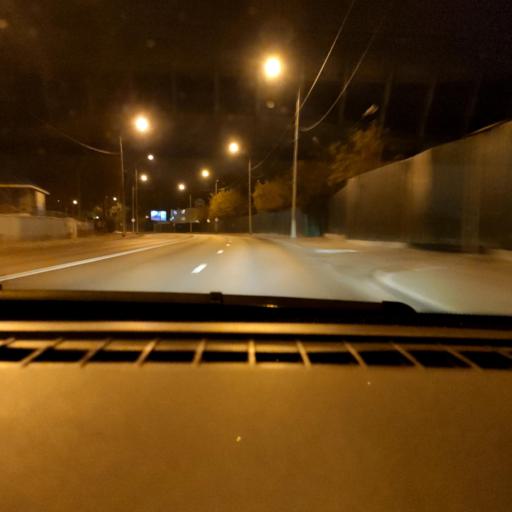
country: RU
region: Voronezj
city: Voronezh
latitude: 51.6866
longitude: 39.2299
